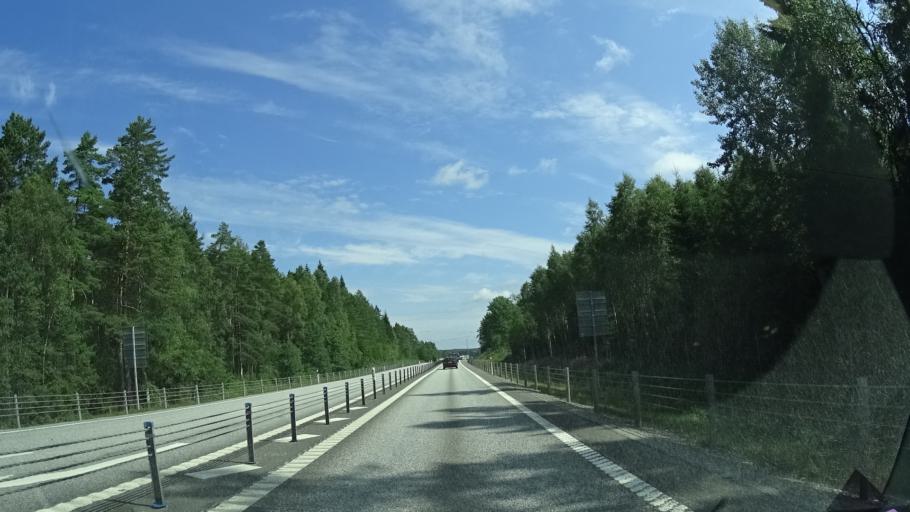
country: SE
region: OErebro
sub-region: Degerfors Kommun
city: Degerfors
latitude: 59.3200
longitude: 14.3467
